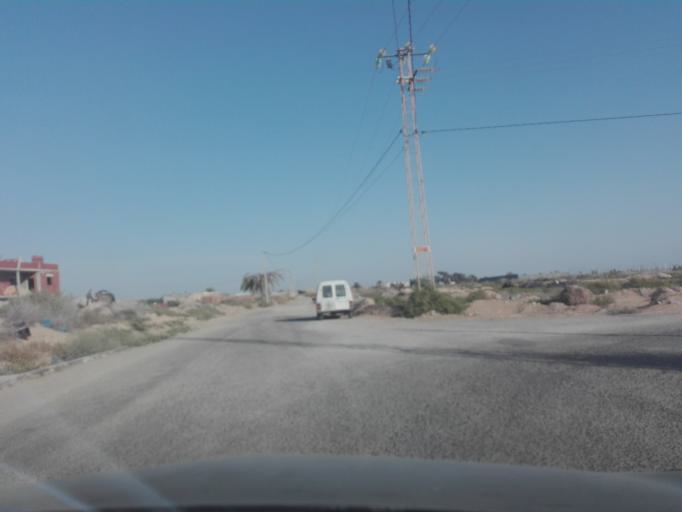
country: TN
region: Qabis
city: Gabes
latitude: 33.9574
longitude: 10.0634
